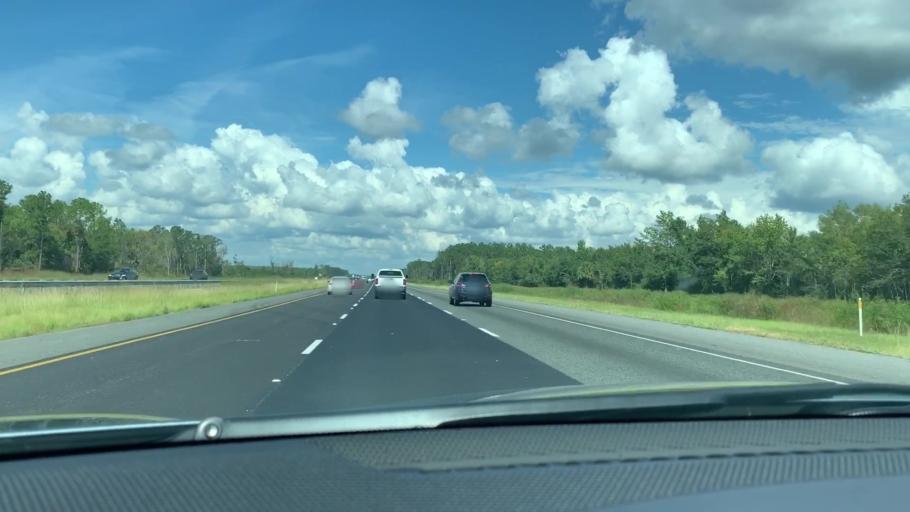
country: US
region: Georgia
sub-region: Camden County
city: Woodbine
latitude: 30.9925
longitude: -81.6654
